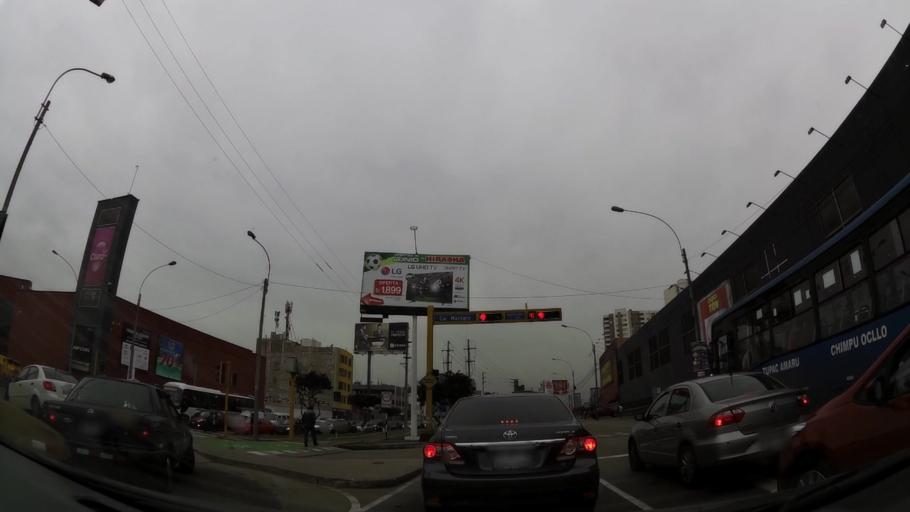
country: PE
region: Callao
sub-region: Callao
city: Callao
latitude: -12.0766
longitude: -77.0806
